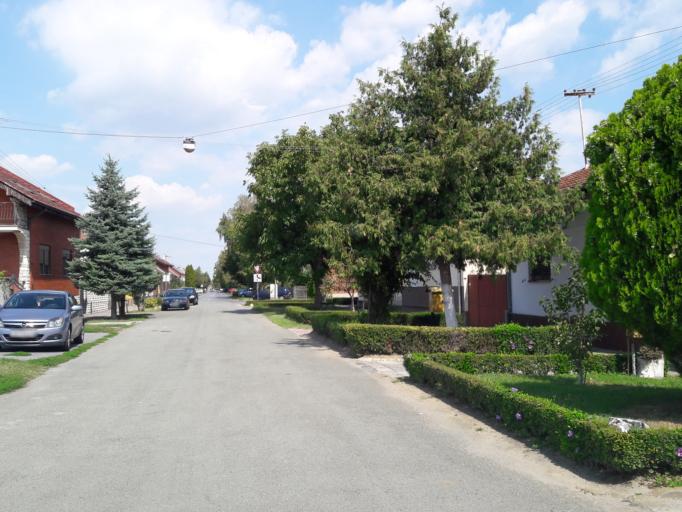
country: HR
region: Osjecko-Baranjska
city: Visnjevac
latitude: 45.5570
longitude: 18.6477
